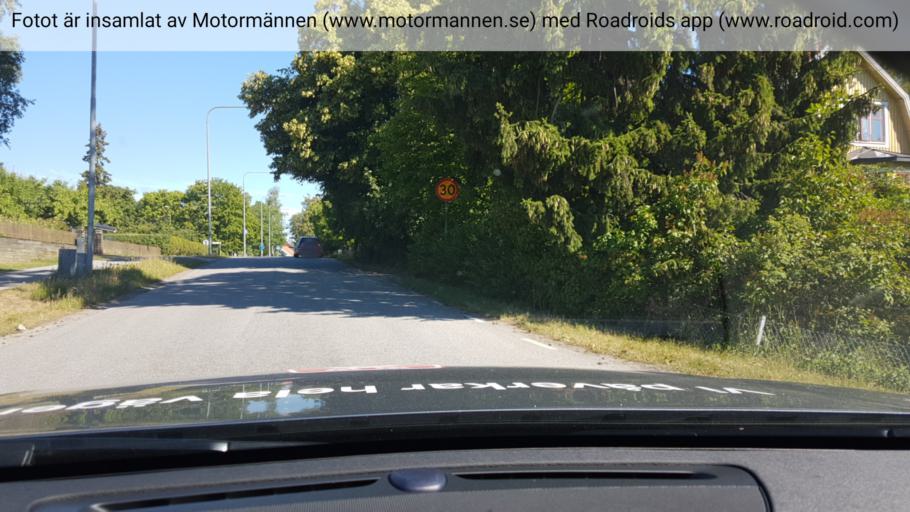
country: SE
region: Stockholm
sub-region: Huddinge Kommun
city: Huddinge
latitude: 59.2360
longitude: 17.9954
